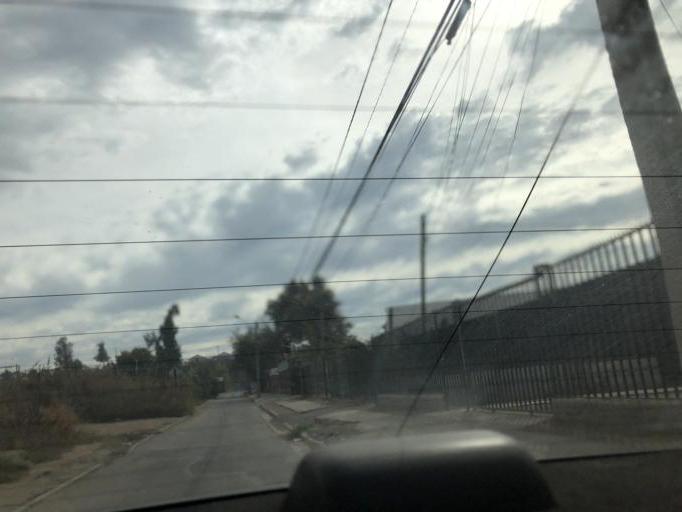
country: CL
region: Santiago Metropolitan
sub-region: Provincia de Cordillera
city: Puente Alto
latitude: -33.6096
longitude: -70.5379
